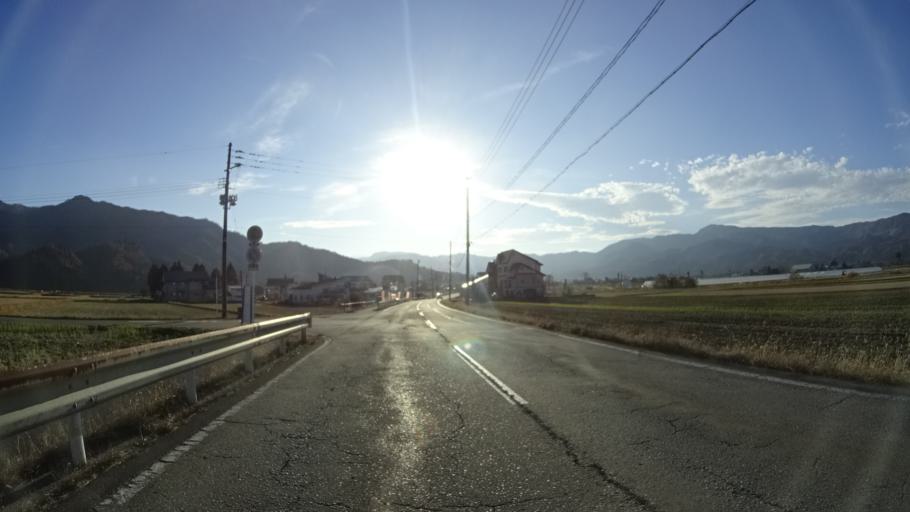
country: JP
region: Niigata
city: Shiozawa
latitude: 37.0122
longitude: 138.8533
